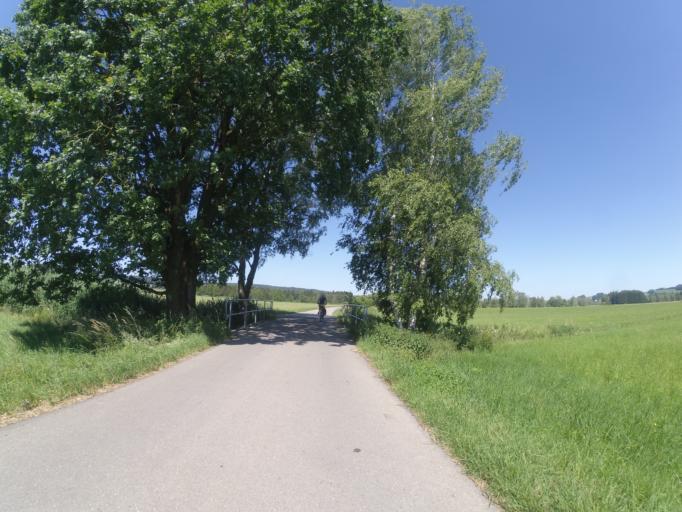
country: DE
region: Baden-Wuerttemberg
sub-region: Tuebingen Region
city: Bad Wurzach
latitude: 47.8726
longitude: 9.9286
